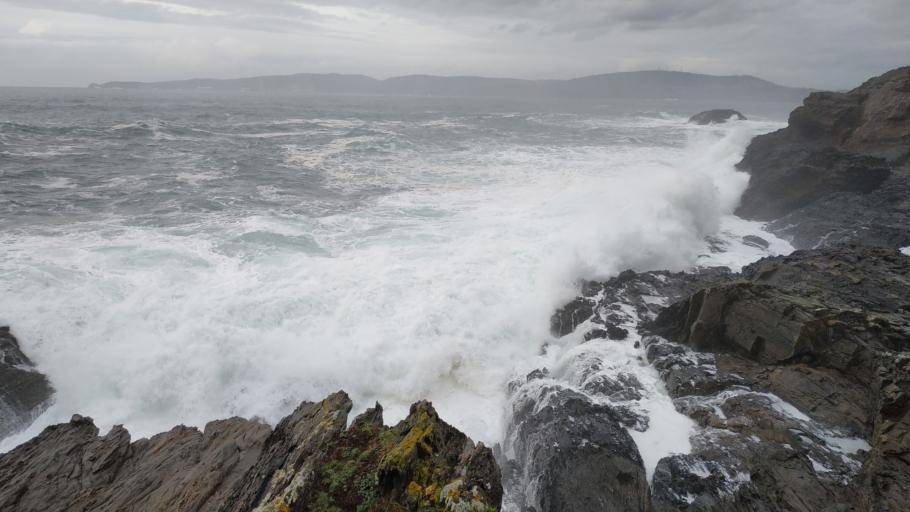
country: ES
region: Galicia
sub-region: Provincia da Coruna
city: Oleiros
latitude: 43.4018
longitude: -8.3301
